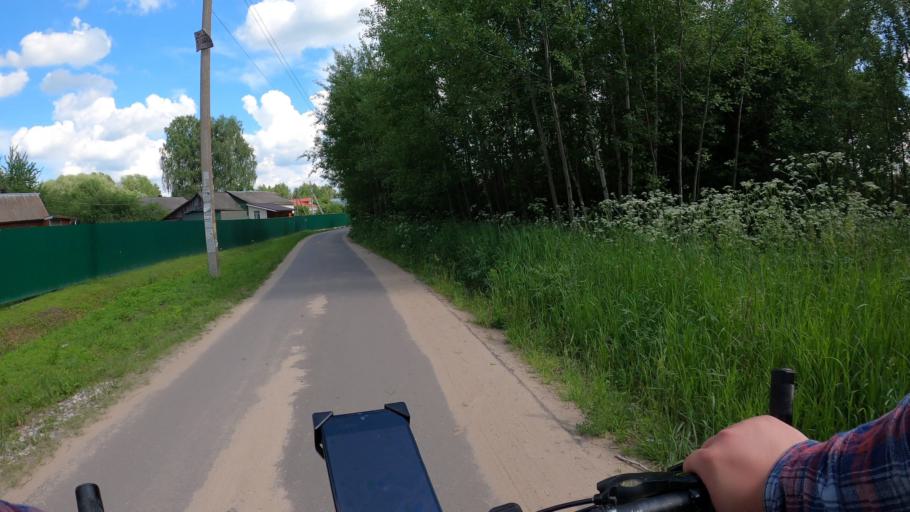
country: RU
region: Moskovskaya
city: Konobeyevo
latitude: 55.3974
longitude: 38.6779
